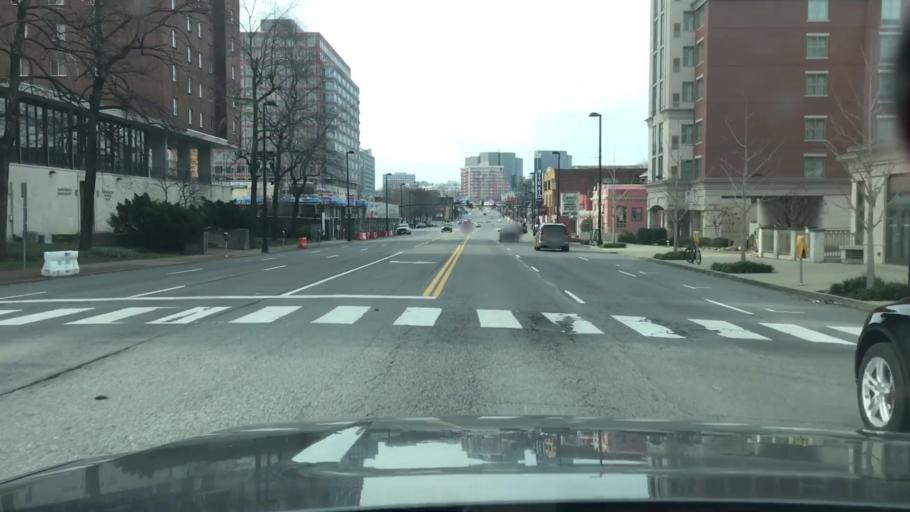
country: US
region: Tennessee
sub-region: Davidson County
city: Nashville
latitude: 36.1479
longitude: -86.8065
